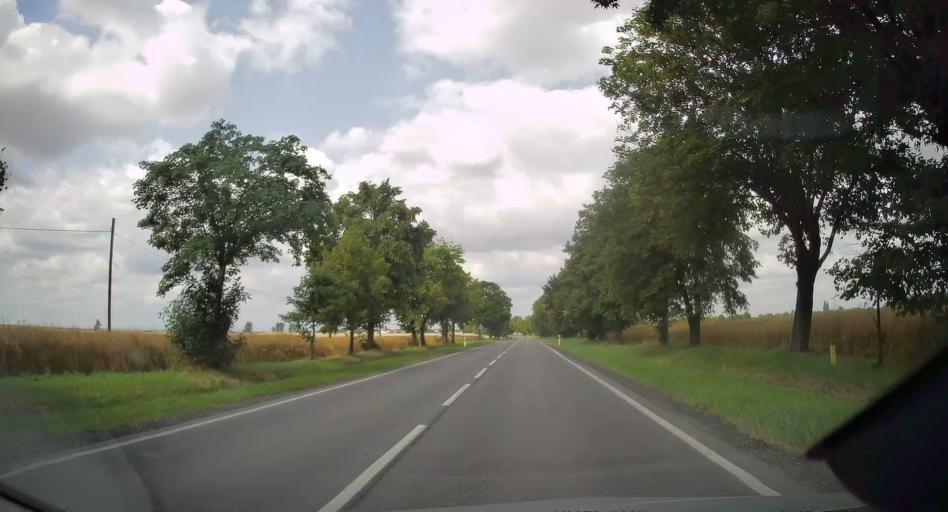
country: PL
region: Opole Voivodeship
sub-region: Powiat prudnicki
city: Twardawa
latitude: 50.3413
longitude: 18.0162
